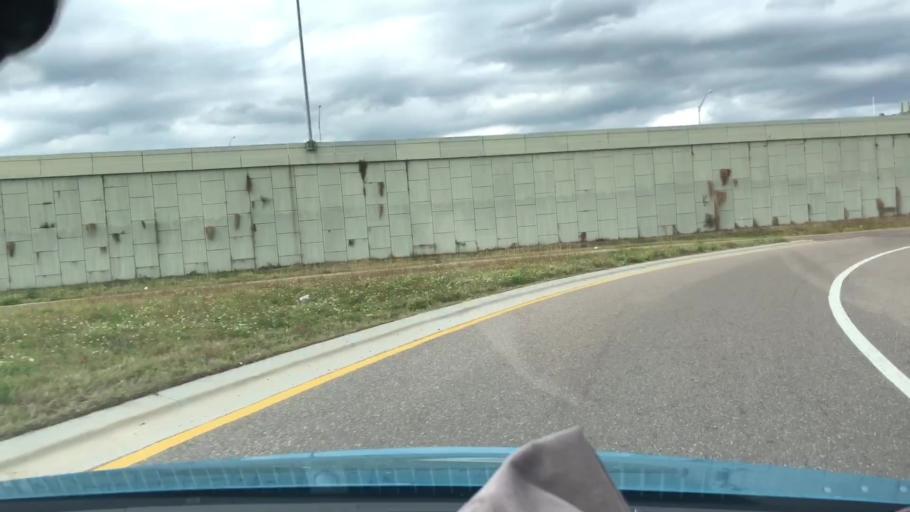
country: US
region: Florida
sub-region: Seminole County
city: Lake Mary
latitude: 28.8117
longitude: -81.3368
